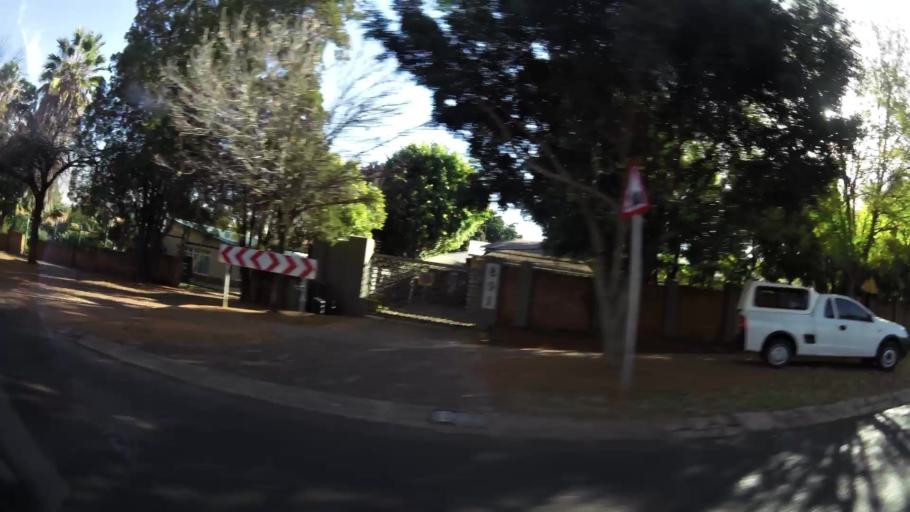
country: ZA
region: Gauteng
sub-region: City of Tshwane Metropolitan Municipality
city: Pretoria
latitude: -25.6967
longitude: 28.2427
